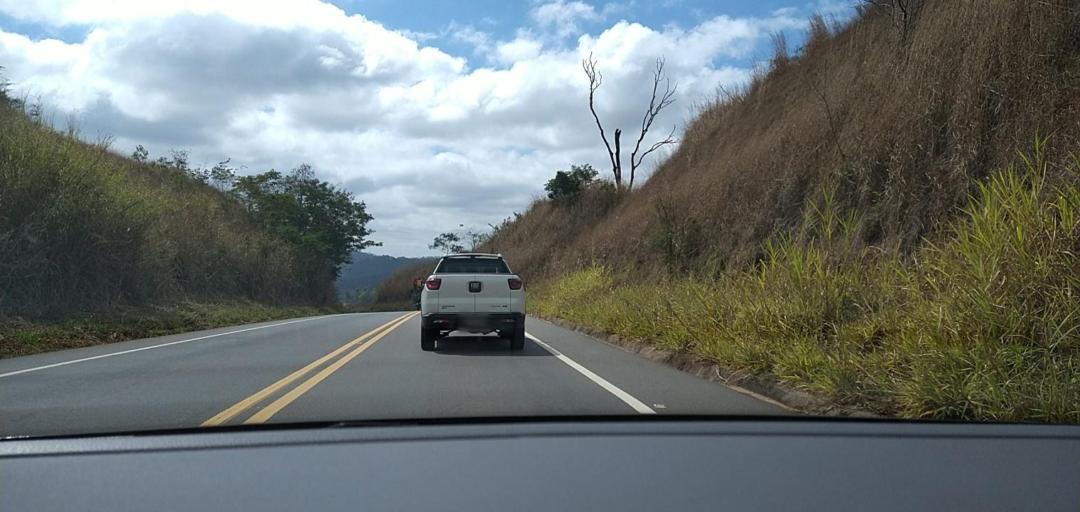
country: BR
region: Minas Gerais
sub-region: Ponte Nova
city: Ponte Nova
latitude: -20.5119
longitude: -42.8859
